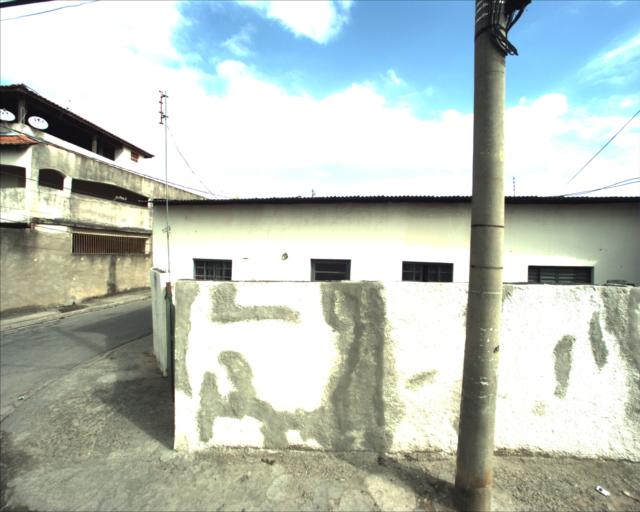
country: BR
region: Sao Paulo
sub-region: Sorocaba
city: Sorocaba
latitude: -23.4968
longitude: -47.4885
